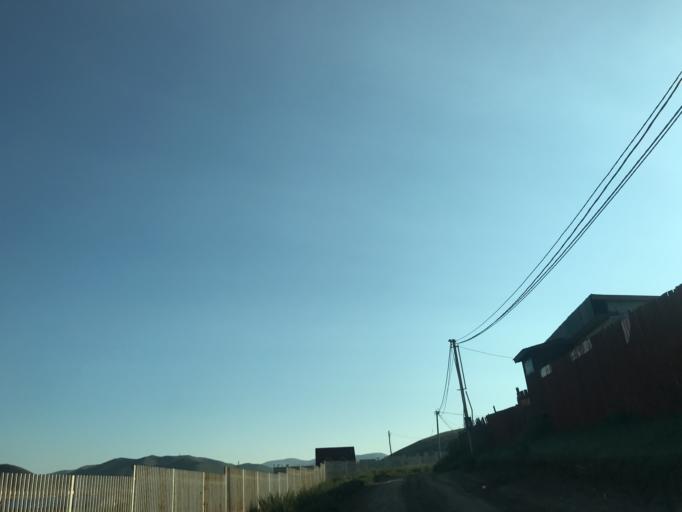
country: MN
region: Ulaanbaatar
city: Ulaanbaatar
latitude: 47.9922
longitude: 106.9668
